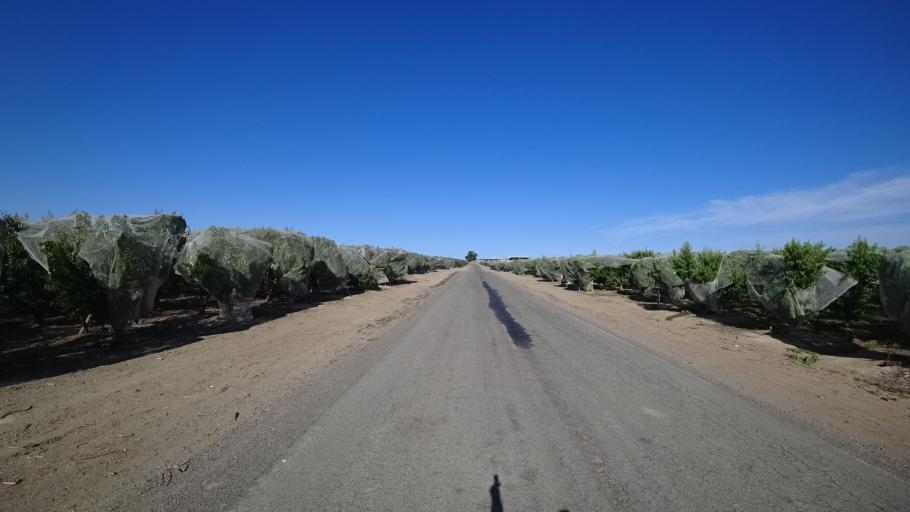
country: US
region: California
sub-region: Kings County
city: Kettleman City
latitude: 36.0096
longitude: -119.9807
